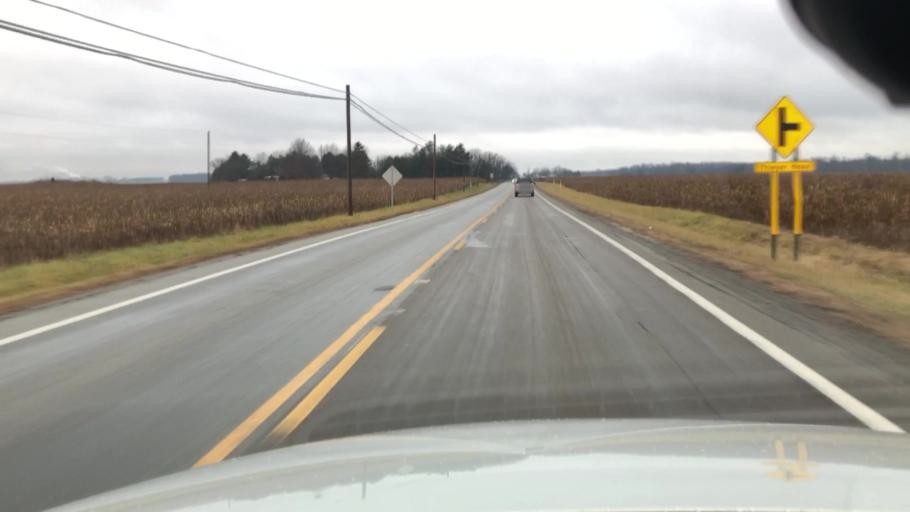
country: US
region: Ohio
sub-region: Allen County
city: Lima
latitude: 40.7097
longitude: -84.0104
